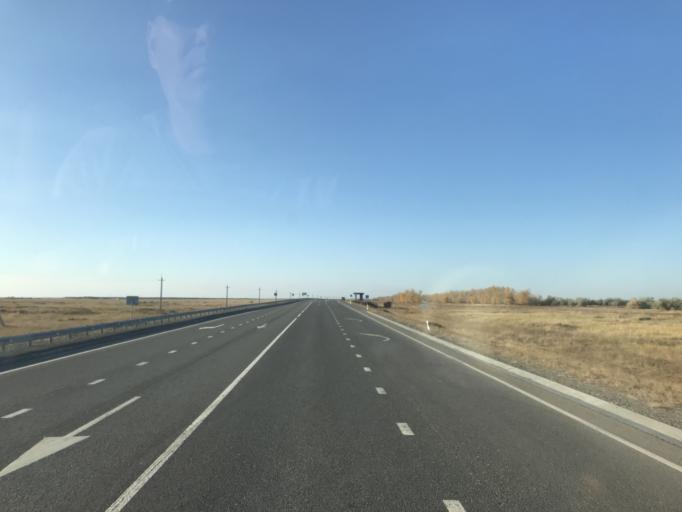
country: KZ
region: Pavlodar
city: Koktobe
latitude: 51.9267
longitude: 77.3338
